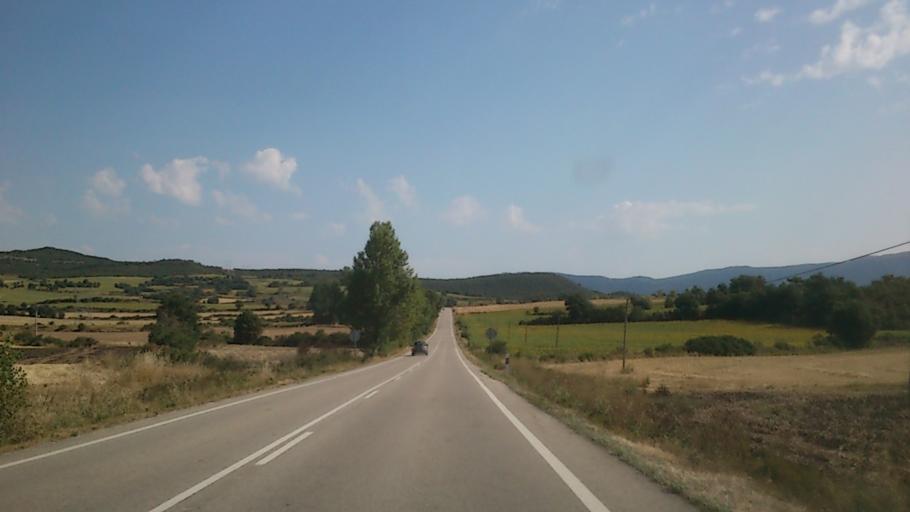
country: ES
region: Castille and Leon
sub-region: Provincia de Burgos
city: Trespaderne
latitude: 42.8232
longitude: -3.3633
